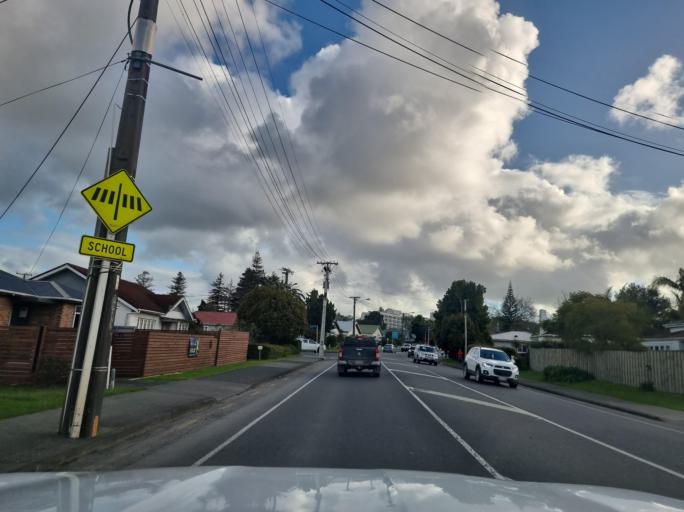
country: NZ
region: Northland
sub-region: Whangarei
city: Whangarei
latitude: -35.7333
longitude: 174.3078
